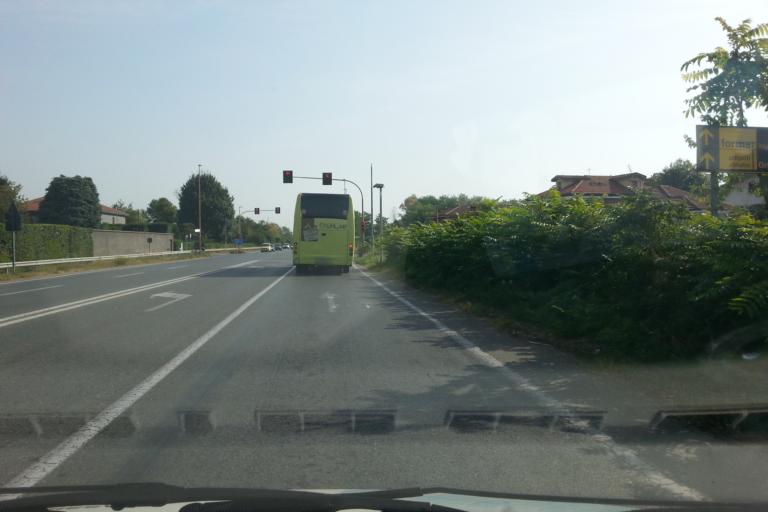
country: IT
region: Piedmont
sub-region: Provincia di Torino
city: Gerbole-Zucche
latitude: 44.9920
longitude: 7.5152
